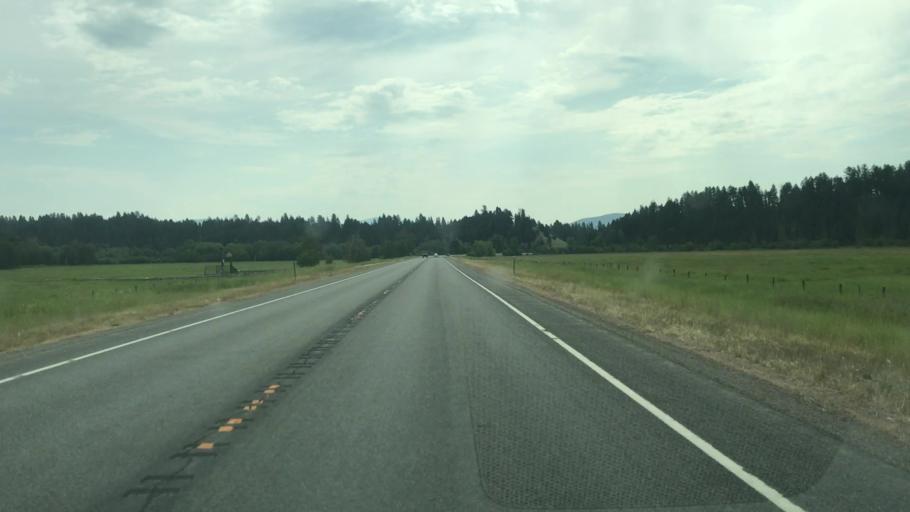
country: US
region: Montana
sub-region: Lewis and Clark County
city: Lincoln
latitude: 47.0169
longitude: -113.0792
